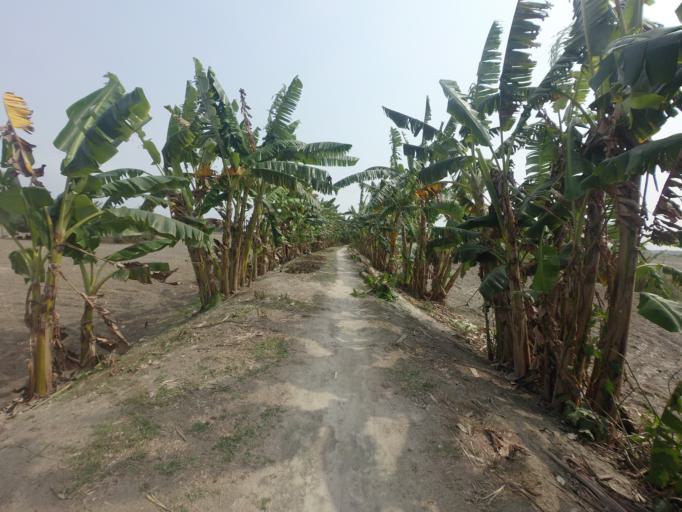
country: BD
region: Rajshahi
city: Sirajganj
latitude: 24.3464
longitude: 89.7287
